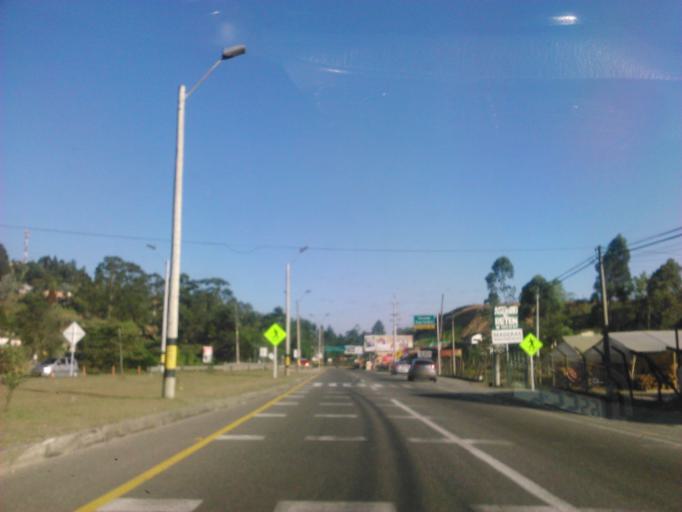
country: CO
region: Antioquia
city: Guarne
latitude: 6.2921
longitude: -75.4503
